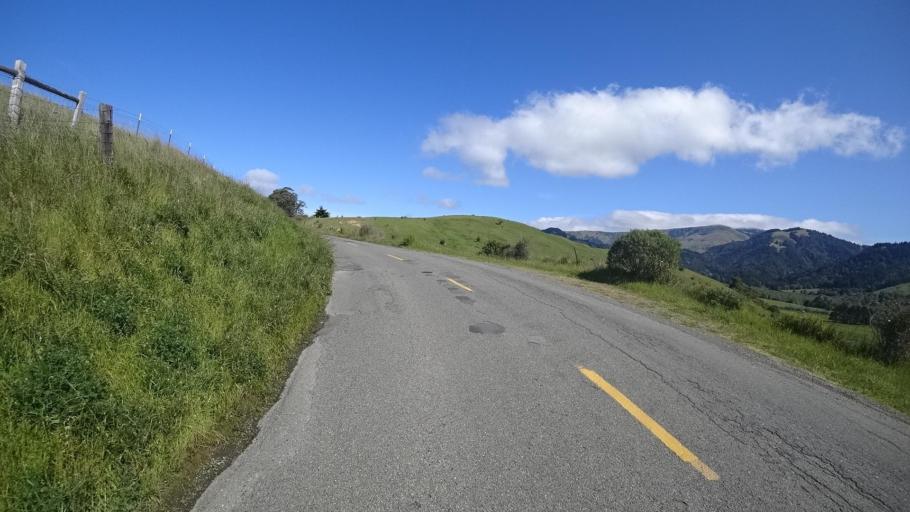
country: US
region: California
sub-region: Humboldt County
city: Ferndale
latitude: 40.3318
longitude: -124.3006
